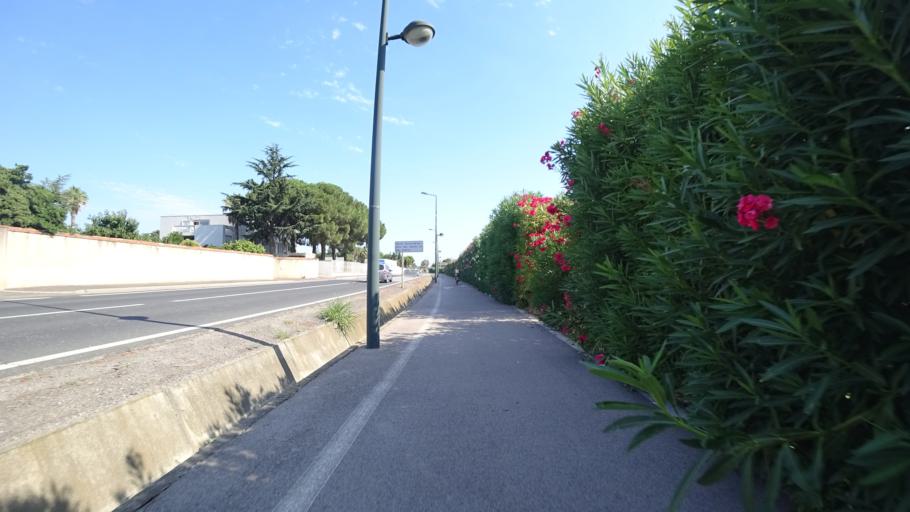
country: FR
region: Languedoc-Roussillon
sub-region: Departement des Pyrenees-Orientales
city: Bompas
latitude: 42.7187
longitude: 2.9323
